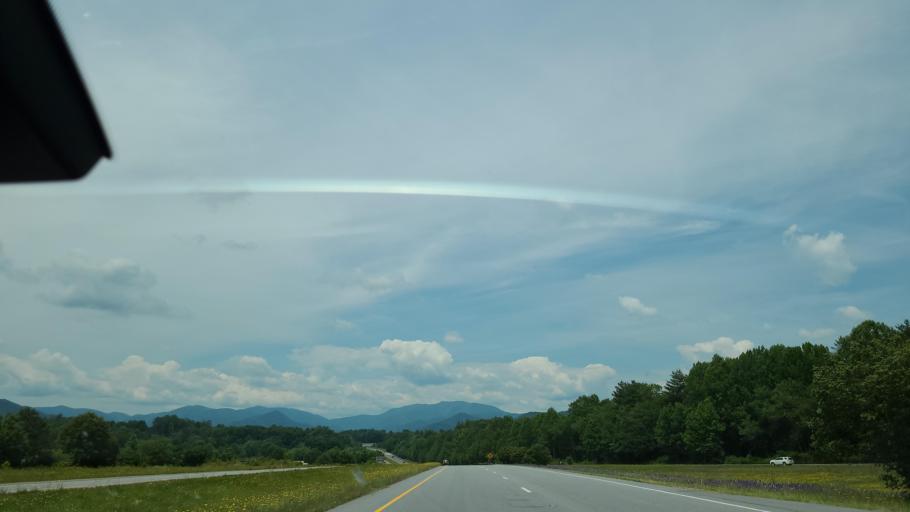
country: US
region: North Carolina
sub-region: Macon County
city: Franklin
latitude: 35.1667
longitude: -83.3919
